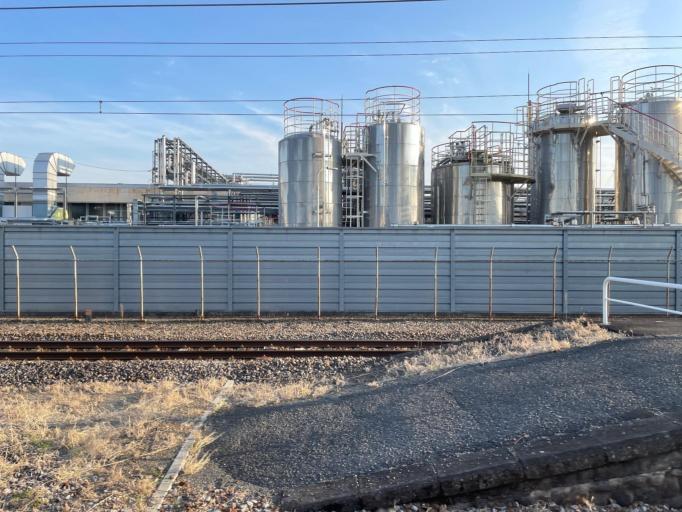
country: JP
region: Gunma
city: Takasaki
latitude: 36.3377
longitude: 138.9586
